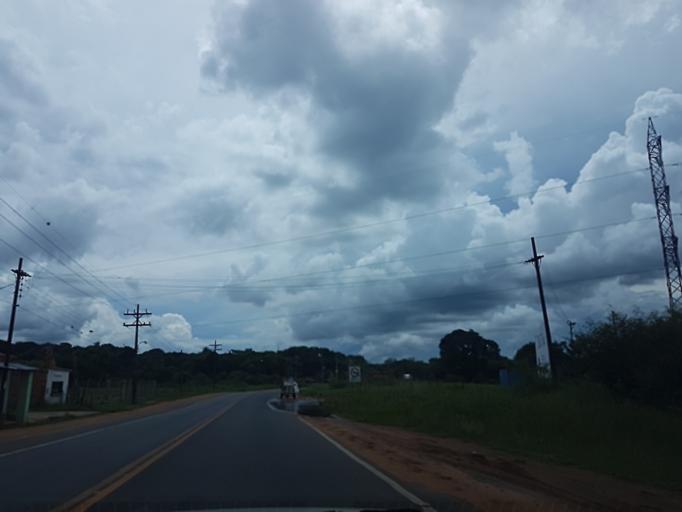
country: PY
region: Central
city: Limpio
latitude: -25.2369
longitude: -57.4387
